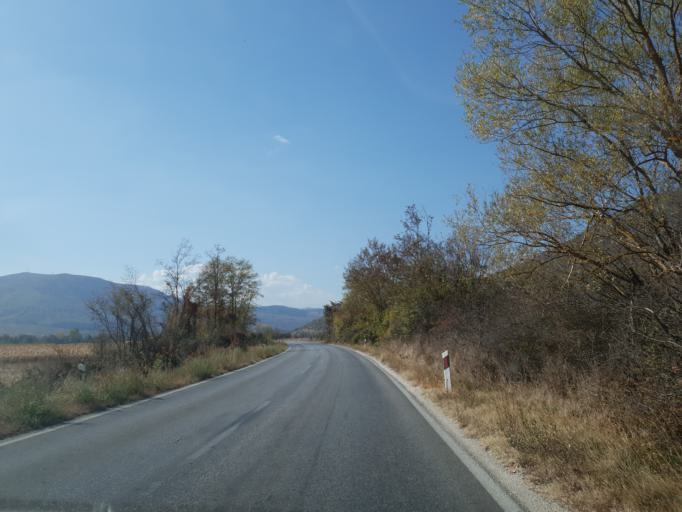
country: MK
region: Plasnica
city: Lisicani
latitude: 41.4703
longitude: 21.0418
